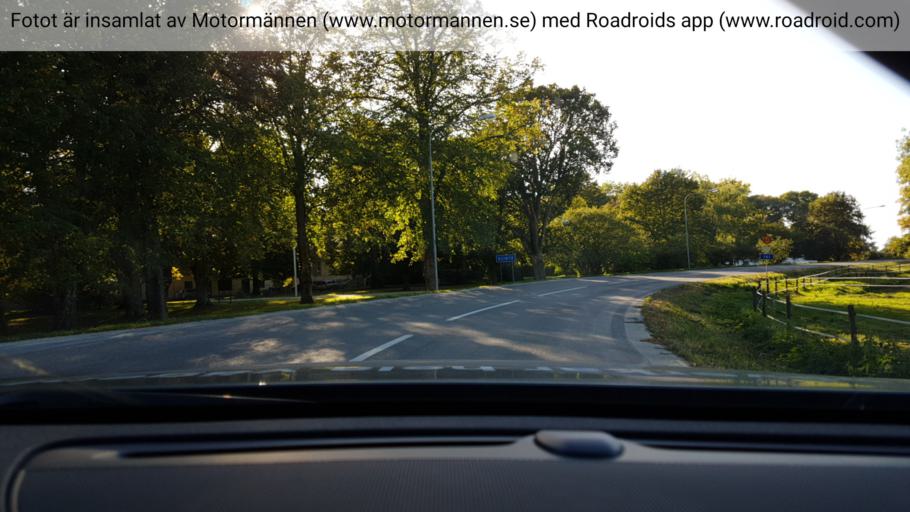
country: SE
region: Gotland
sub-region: Gotland
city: Klintehamn
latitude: 57.3791
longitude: 18.2331
